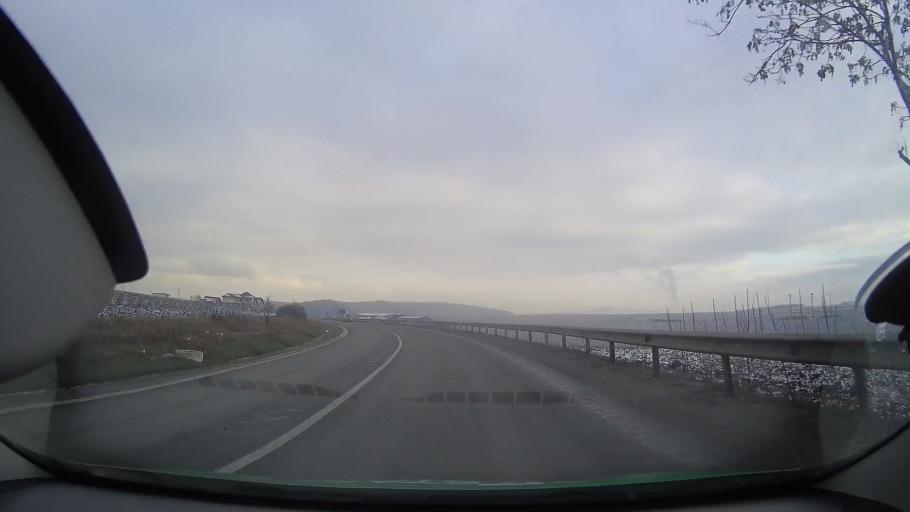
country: RO
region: Mures
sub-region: Comuna Ludus
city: Ludus
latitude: 46.4786
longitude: 24.1226
